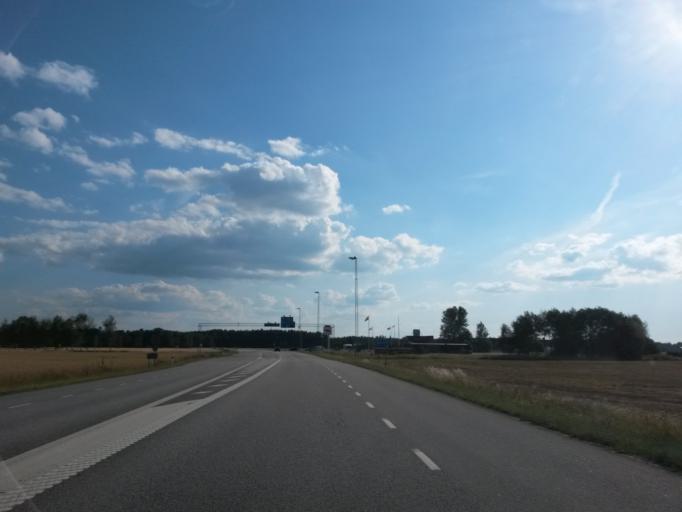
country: SE
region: Vaestra Goetaland
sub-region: Vara Kommun
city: Vara
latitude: 58.2355
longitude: 12.9311
